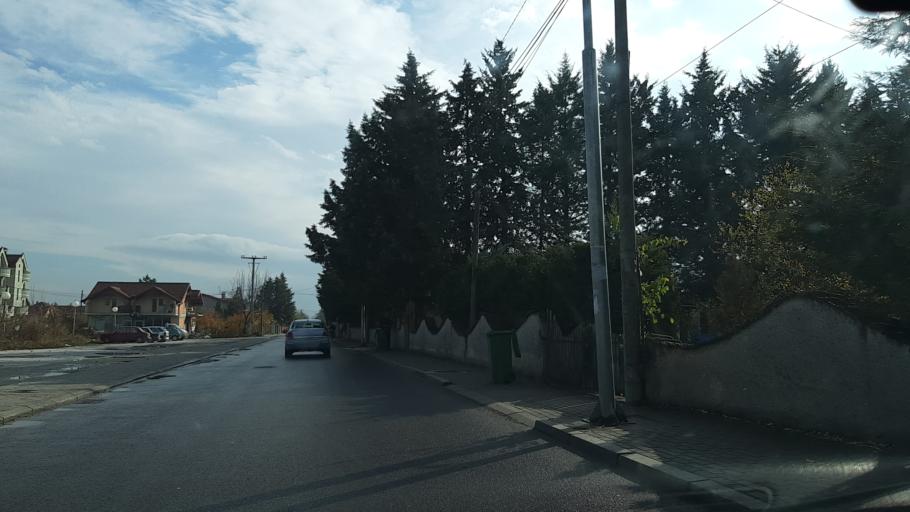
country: MK
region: Kisela Voda
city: Usje
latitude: 41.9792
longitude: 21.4811
